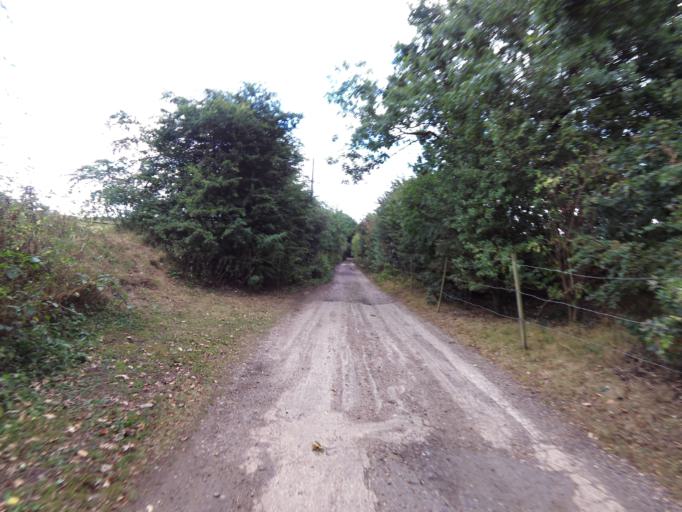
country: GB
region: England
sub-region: Hertfordshire
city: Radlett
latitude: 51.7081
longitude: -0.3234
